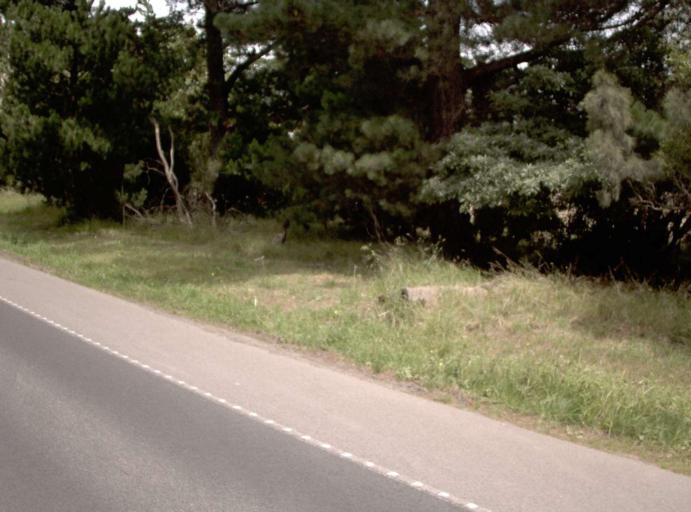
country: AU
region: Victoria
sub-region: Mornington Peninsula
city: Tyabb
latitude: -38.2660
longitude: 145.1981
